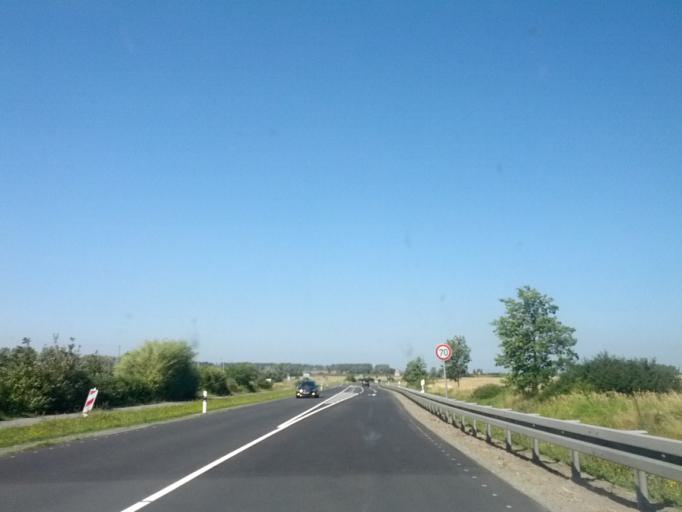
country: DE
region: Mecklenburg-Vorpommern
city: Sagard
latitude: 54.5046
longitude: 13.5515
